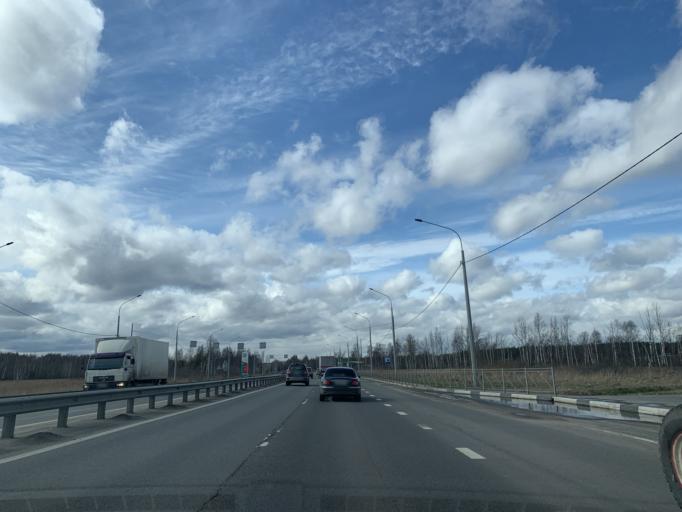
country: RU
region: Jaroslavl
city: Yaroslavl
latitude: 57.6718
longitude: 39.9449
